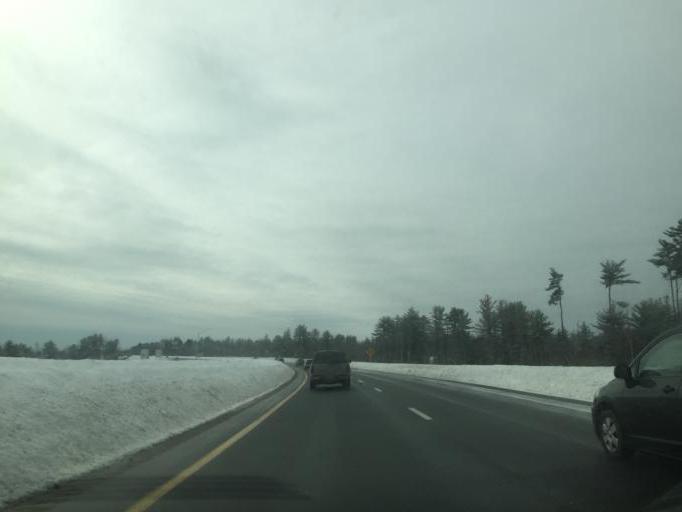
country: US
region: New Hampshire
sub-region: Strafford County
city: Rochester
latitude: 43.3180
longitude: -70.9961
